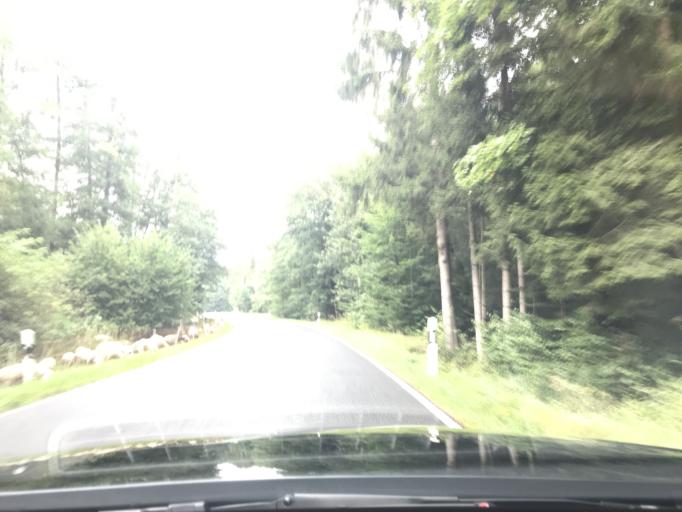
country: DE
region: Bavaria
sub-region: Regierungsbezirk Unterfranken
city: Breitbrunn
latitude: 50.0139
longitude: 10.6769
